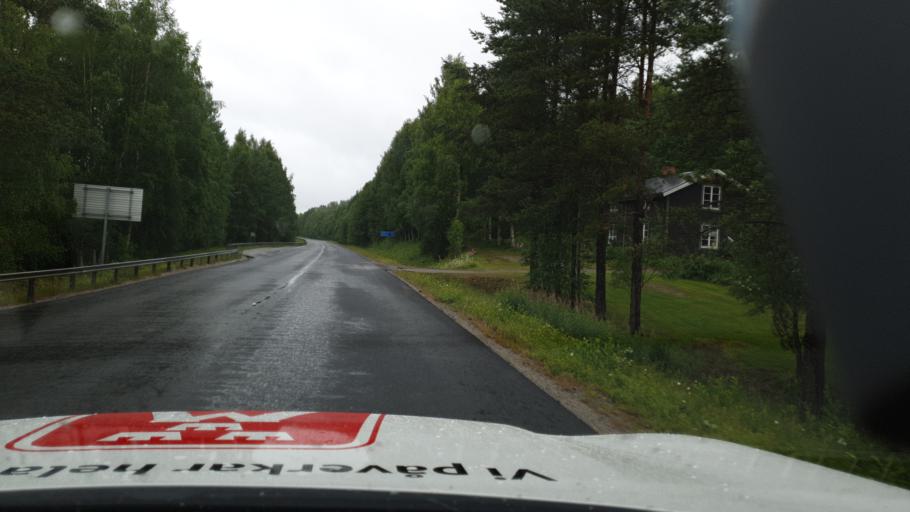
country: SE
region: Vaesterbotten
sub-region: Vindelns Kommun
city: Vindeln
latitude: 64.2960
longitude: 19.6194
